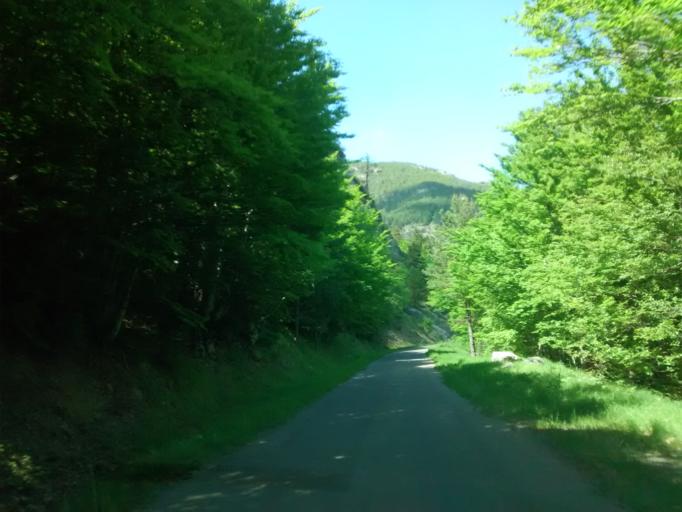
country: ES
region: Aragon
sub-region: Provincia de Huesca
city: Canfranc
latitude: 42.7320
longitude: -0.5955
